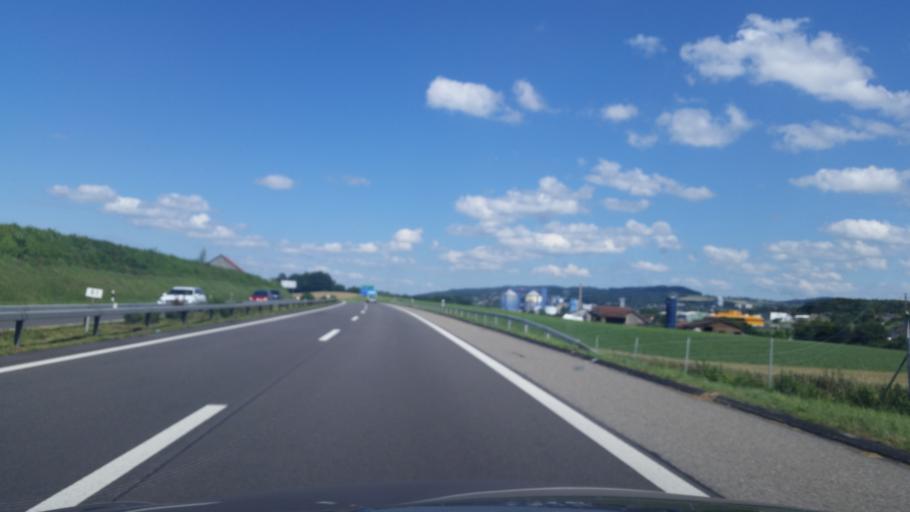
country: CH
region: Thurgau
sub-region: Frauenfeld District
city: Gachnang
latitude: 47.5551
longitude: 8.8549
